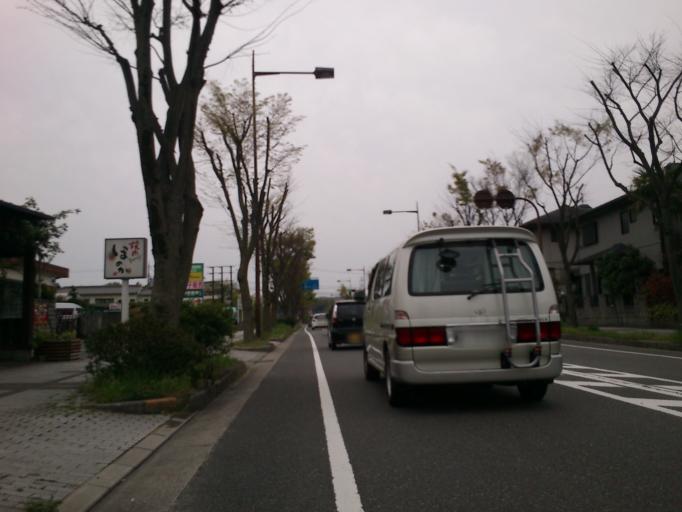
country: JP
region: Kyoto
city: Yawata
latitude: 34.8467
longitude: 135.7129
